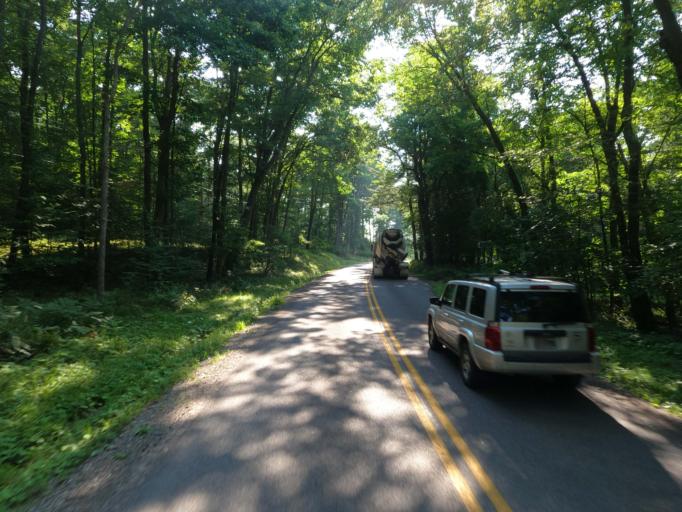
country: US
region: Maryland
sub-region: Garrett County
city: Mountain Lake Park
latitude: 39.4963
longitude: -79.3507
